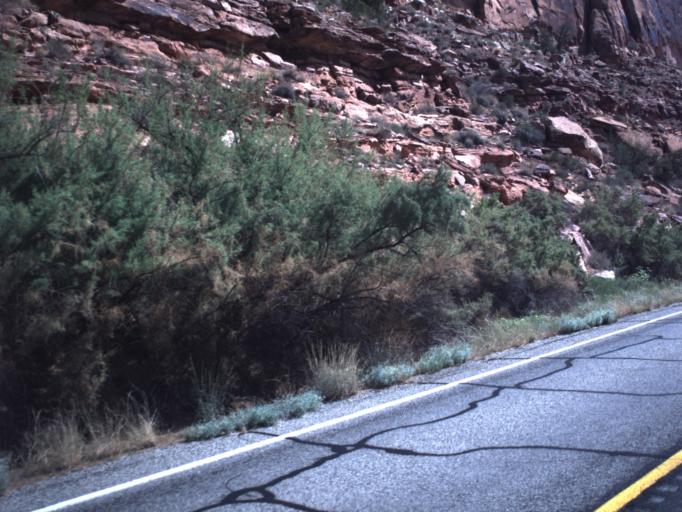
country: US
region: Utah
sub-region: Grand County
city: Moab
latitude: 38.5518
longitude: -109.6312
